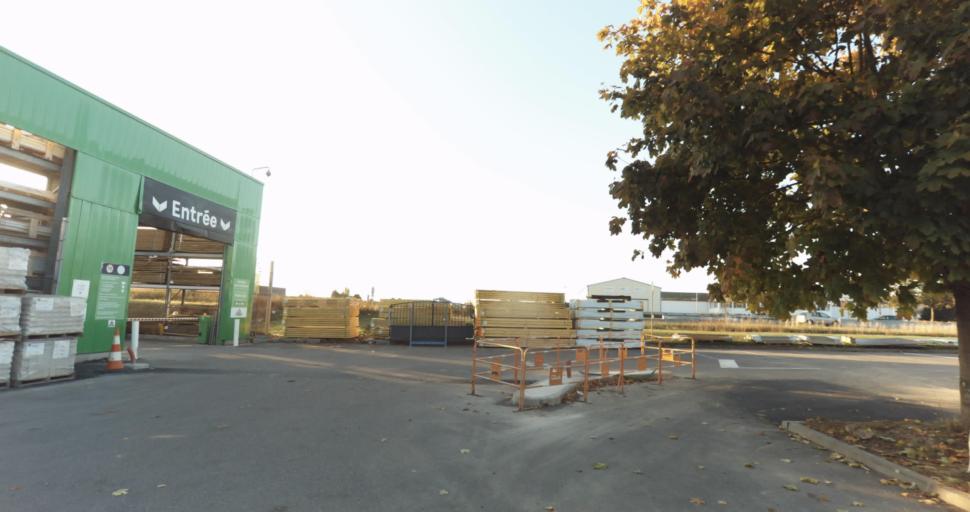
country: FR
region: Centre
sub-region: Departement d'Eure-et-Loir
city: Vernouillet
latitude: 48.7166
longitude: 1.3737
